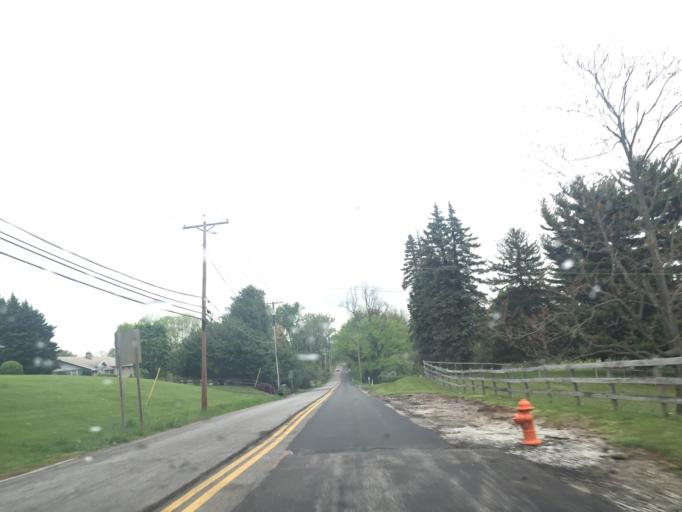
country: US
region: Maryland
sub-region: Baltimore County
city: Catonsville
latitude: 39.2521
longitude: -76.7236
